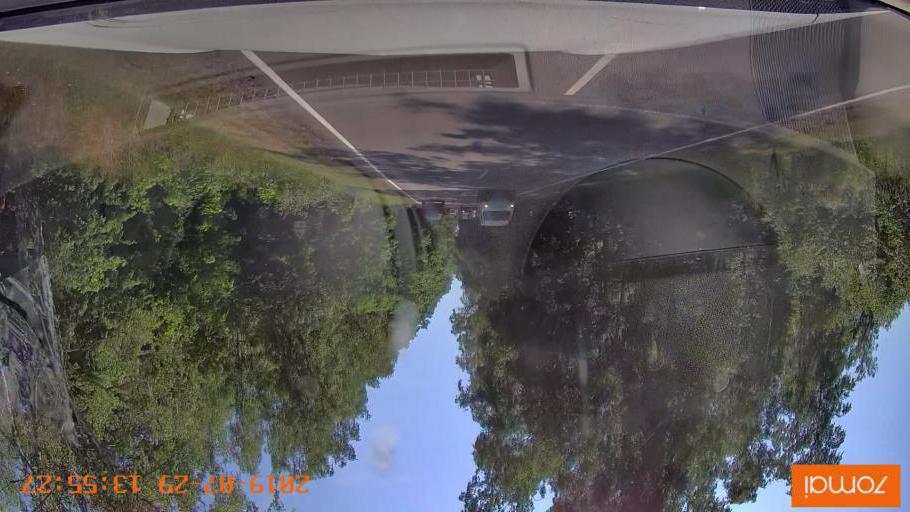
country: RU
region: Kaliningrad
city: Primorsk
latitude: 54.7152
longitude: 19.9569
